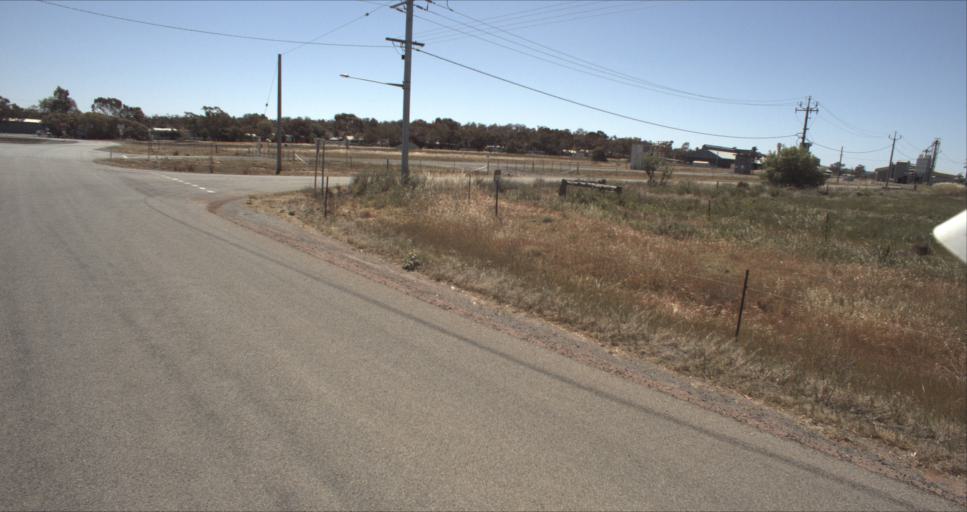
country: AU
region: New South Wales
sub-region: Leeton
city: Leeton
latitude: -34.4280
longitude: 146.3001
